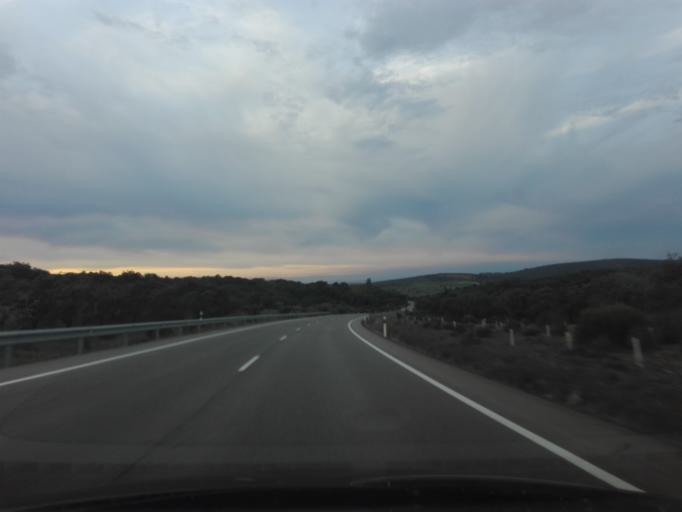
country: ES
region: Extremadura
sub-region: Provincia de Caceres
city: Pedroso de Acim
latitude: 39.8275
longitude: -6.3781
